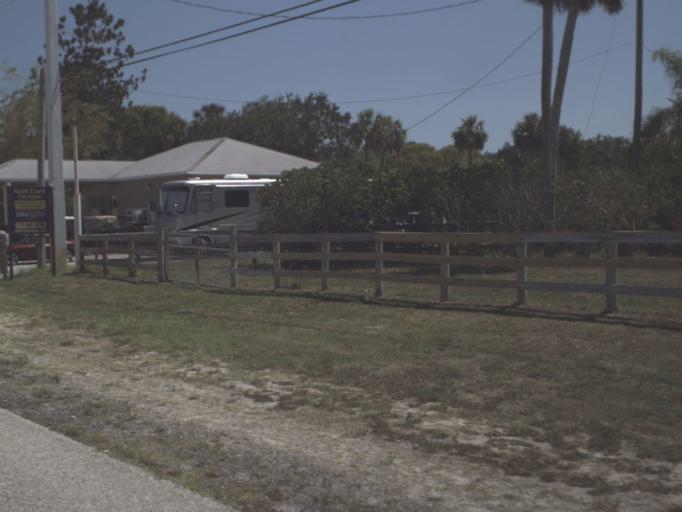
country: US
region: Florida
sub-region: Brevard County
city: Micco
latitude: 27.8788
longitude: -80.5005
